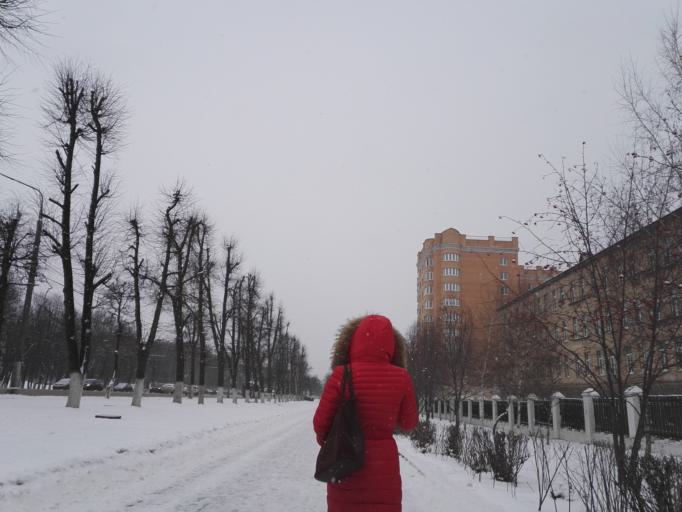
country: RU
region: Tula
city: Mendeleyevskiy
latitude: 54.1702
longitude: 37.5928
